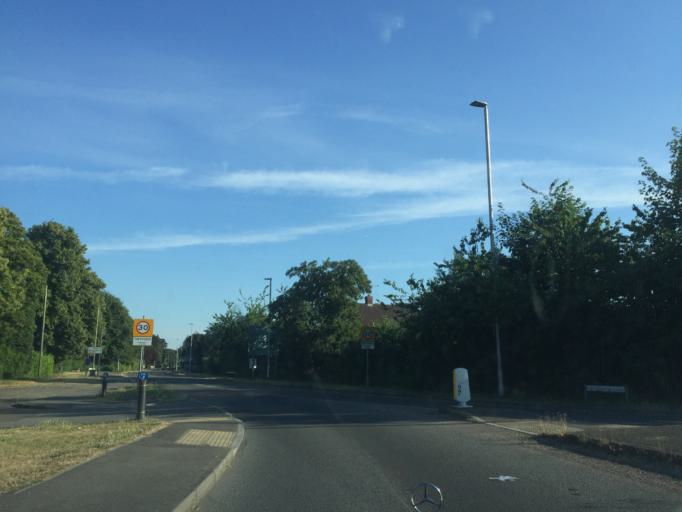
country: GB
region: England
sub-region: Wokingham
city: Twyford
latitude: 51.4864
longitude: -0.8698
